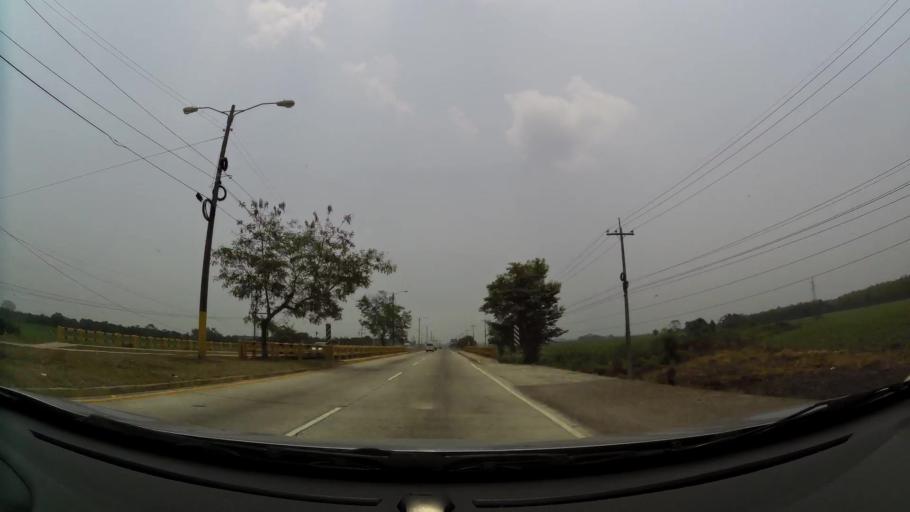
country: HN
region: Cortes
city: La Lima
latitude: 15.4117
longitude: -87.8745
